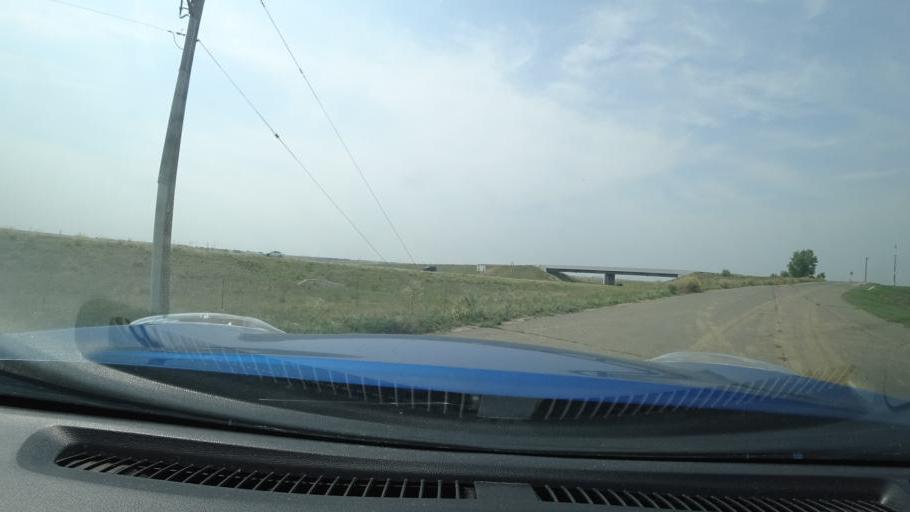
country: US
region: Colorado
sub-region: Adams County
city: Aurora
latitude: 39.7530
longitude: -104.7158
